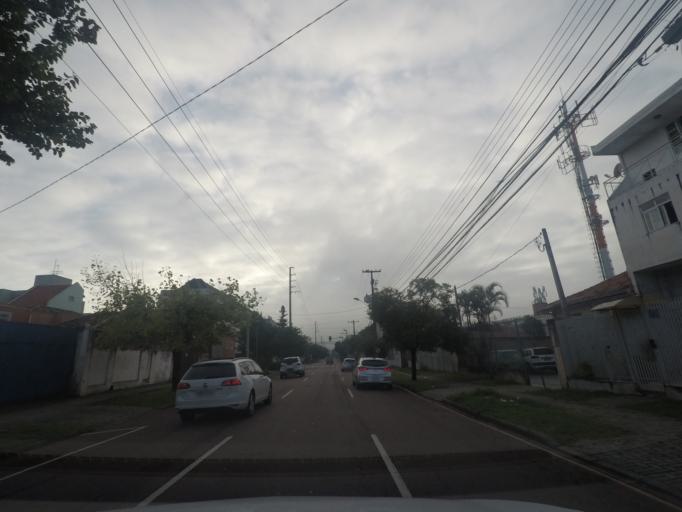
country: BR
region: Parana
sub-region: Curitiba
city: Curitiba
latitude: -25.4449
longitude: -49.2632
